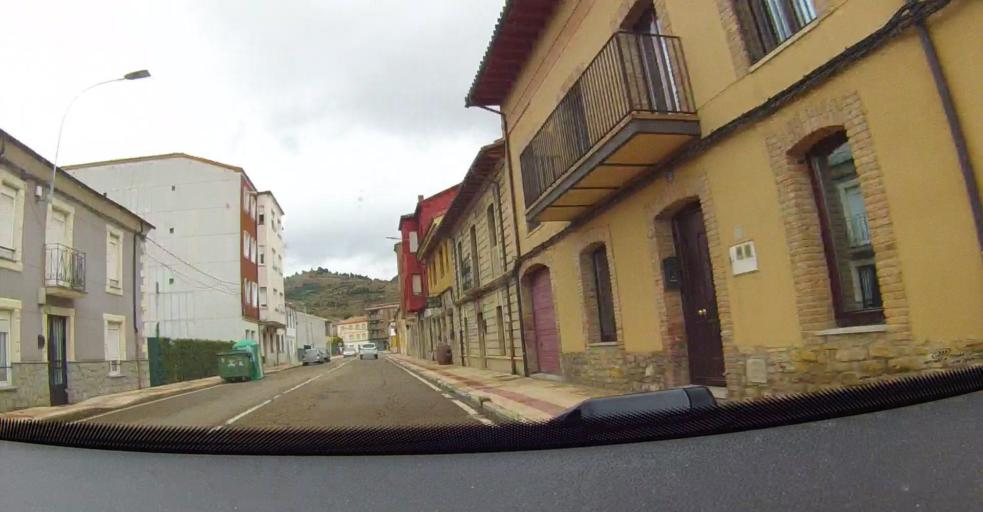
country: ES
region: Castille and Leon
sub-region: Provincia de Leon
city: Cistierna
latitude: 42.7991
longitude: -5.1257
